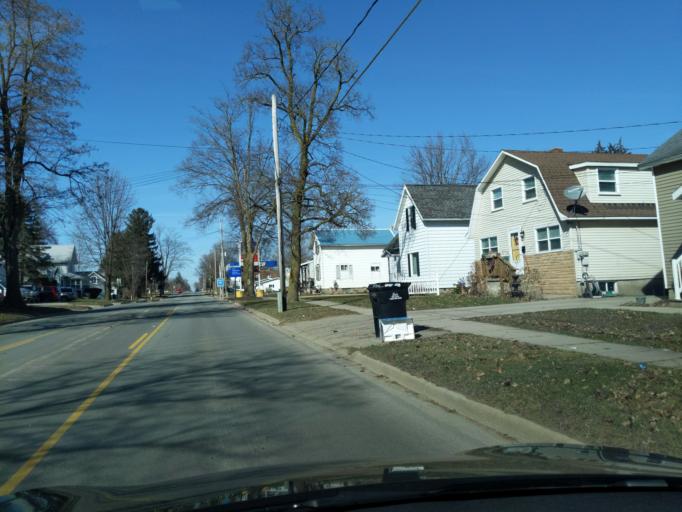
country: US
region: Michigan
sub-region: Ionia County
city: Lake Odessa
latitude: 42.7837
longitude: -85.1333
